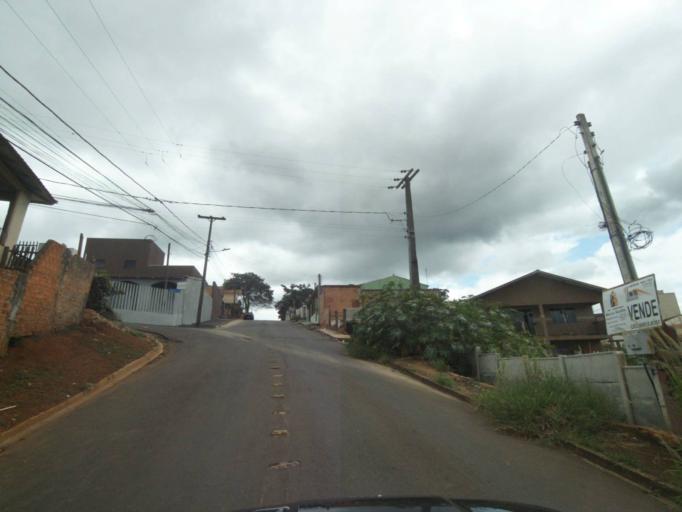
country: BR
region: Parana
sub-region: Telemaco Borba
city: Telemaco Borba
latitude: -24.3243
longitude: -50.6360
